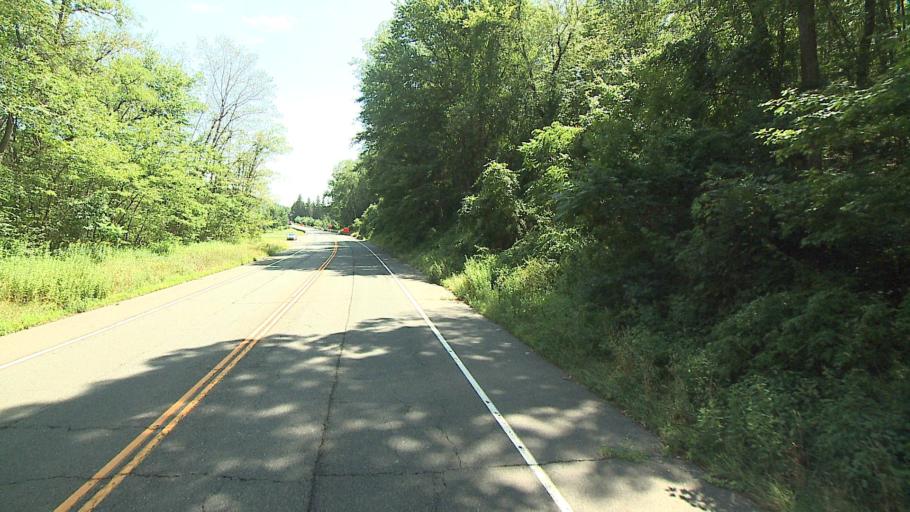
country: US
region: Connecticut
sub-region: Hartford County
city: Collinsville
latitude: 41.7672
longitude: -72.9008
